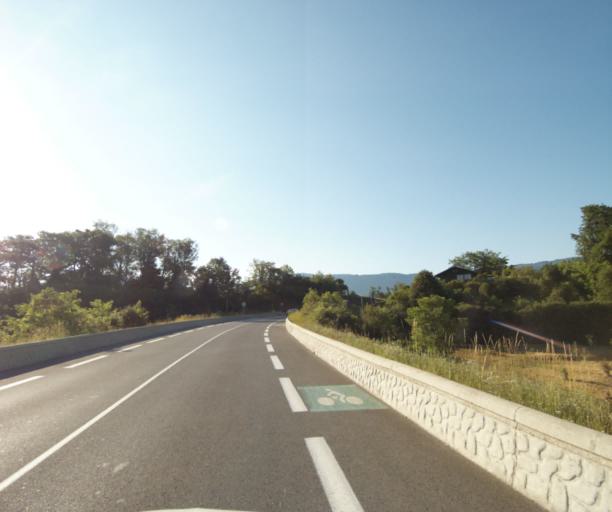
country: FR
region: Rhone-Alpes
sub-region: Departement de la Haute-Savoie
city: Allinges
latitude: 46.3542
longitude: 6.4575
